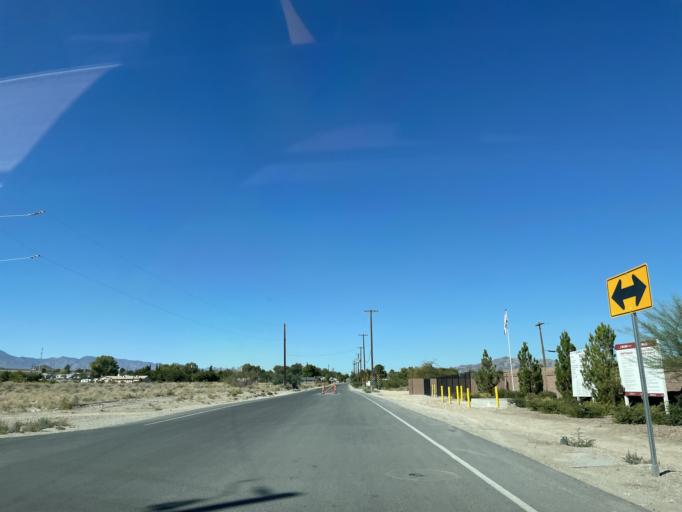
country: US
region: Nevada
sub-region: Nye County
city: Pahrump
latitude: 36.5734
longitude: -115.6657
